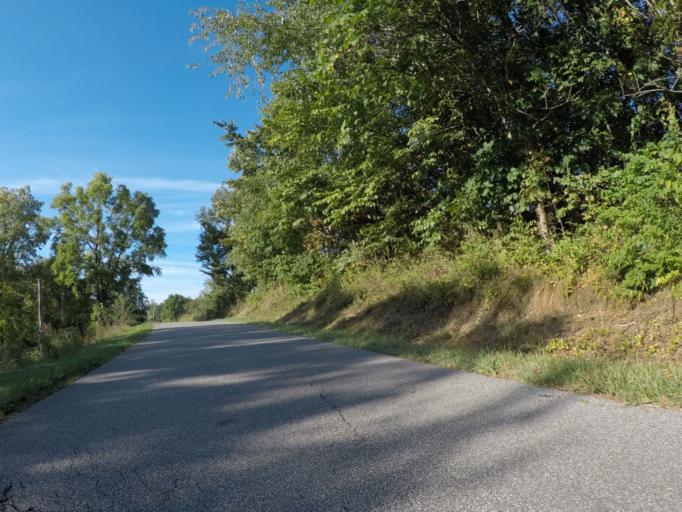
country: US
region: Ohio
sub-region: Lawrence County
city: Coal Grove
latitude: 38.6002
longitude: -82.5558
